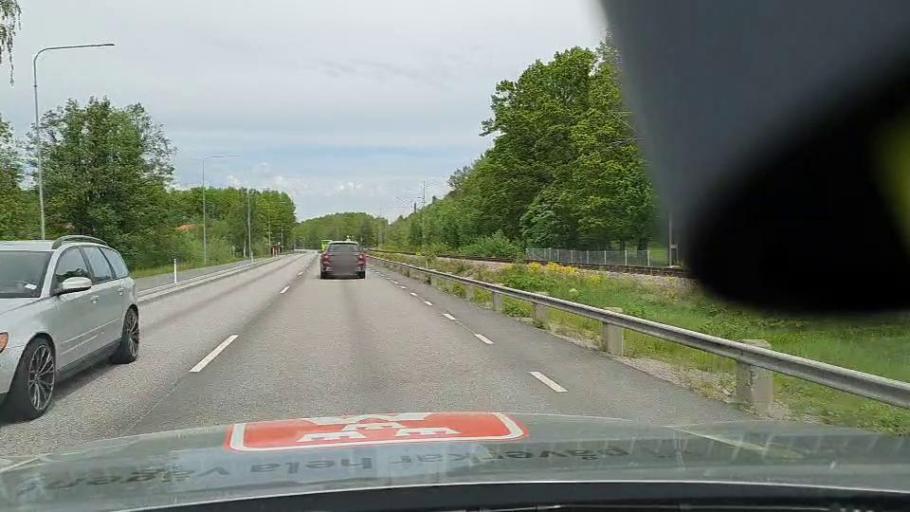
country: SE
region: Soedermanland
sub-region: Flens Kommun
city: Flen
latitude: 59.0723
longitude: 16.5931
